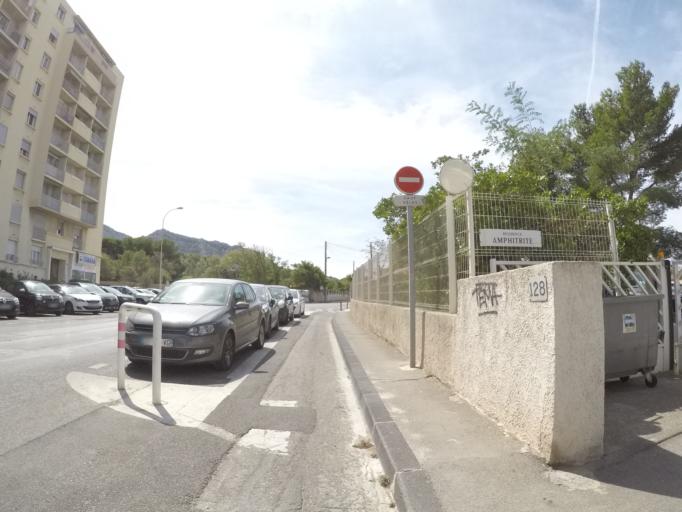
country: FR
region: Provence-Alpes-Cote d'Azur
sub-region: Departement des Bouches-du-Rhone
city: Marseille 08
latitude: 43.2411
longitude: 5.3682
